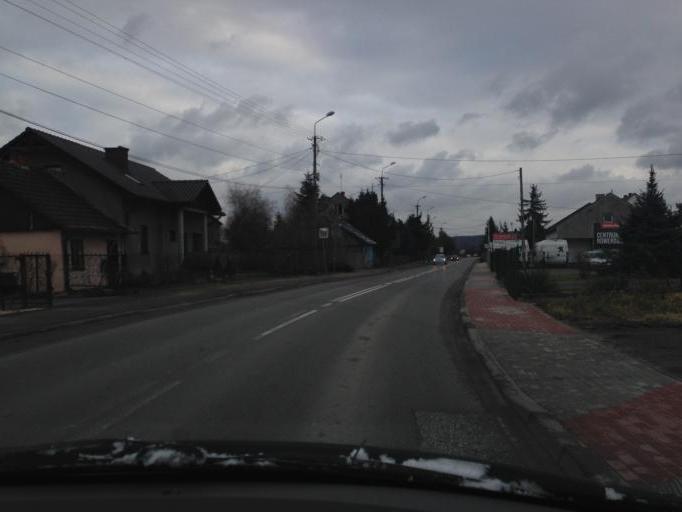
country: PL
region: Lesser Poland Voivodeship
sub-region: Powiat wielicki
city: Gdow
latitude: 49.9065
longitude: 20.2008
